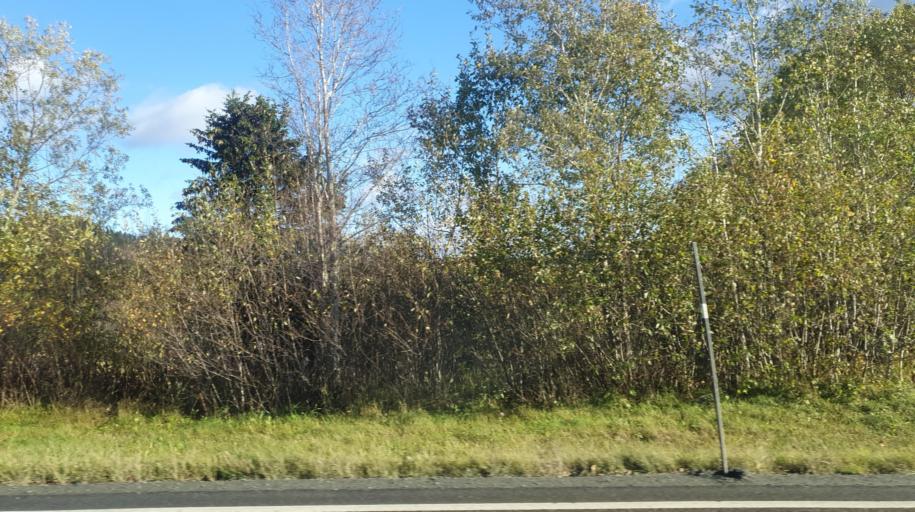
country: NO
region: Sor-Trondelag
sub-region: Klaebu
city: Klaebu
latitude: 63.3126
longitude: 10.4408
